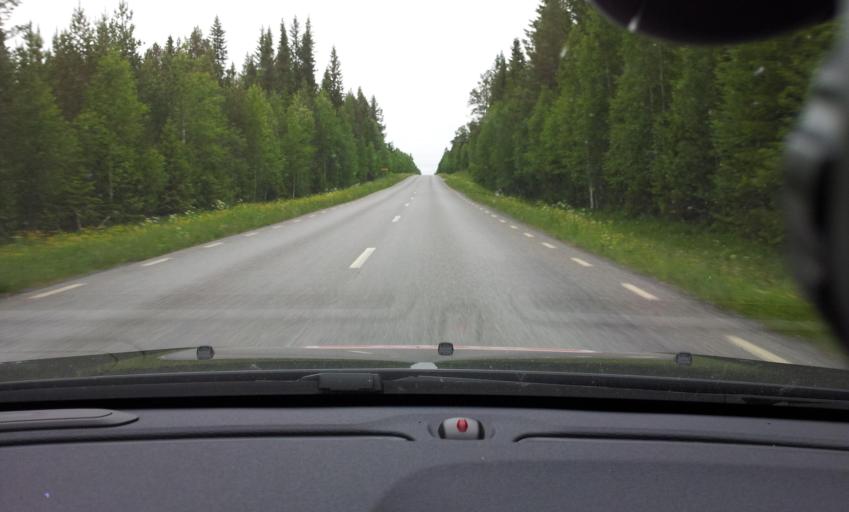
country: SE
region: Jaemtland
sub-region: Krokoms Kommun
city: Valla
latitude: 63.2186
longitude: 14.0233
